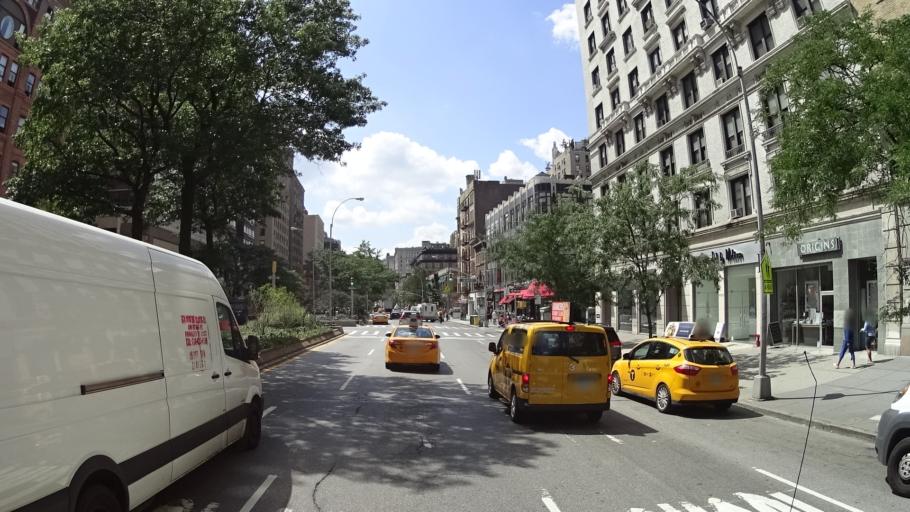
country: US
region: New York
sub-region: New York County
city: Manhattan
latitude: 40.7875
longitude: -73.9773
